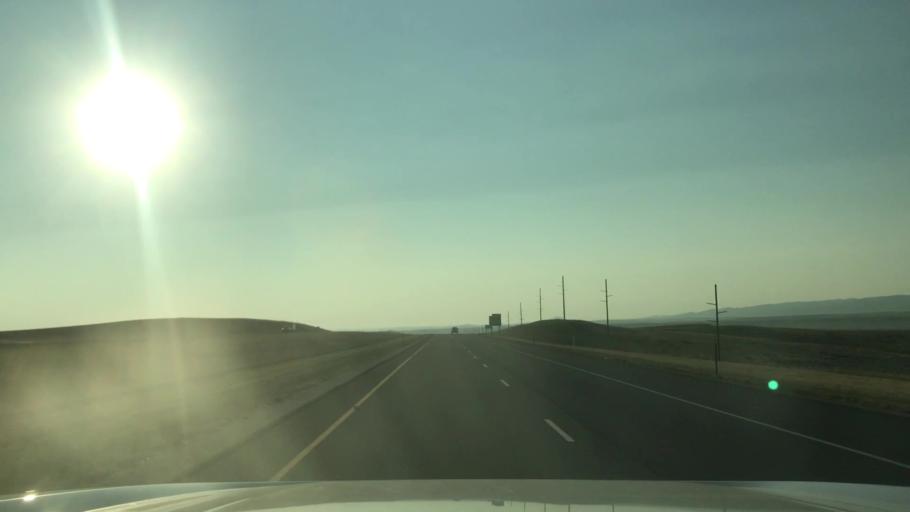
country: US
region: Wyoming
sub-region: Converse County
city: Glenrock
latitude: 42.8401
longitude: -105.9198
